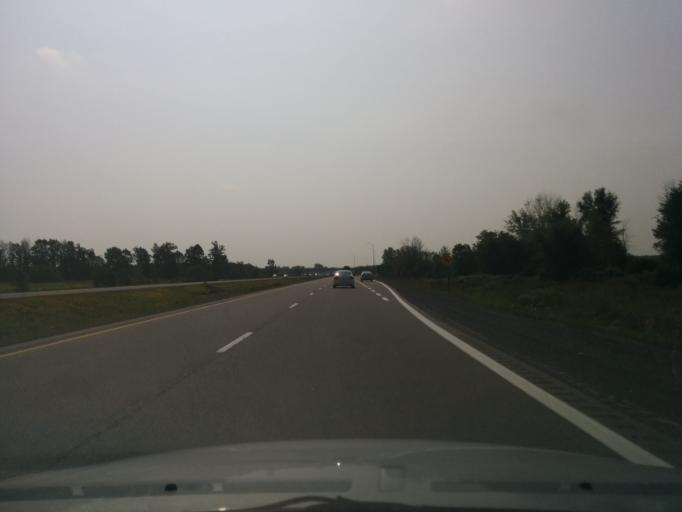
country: CA
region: Ontario
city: Bells Corners
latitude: 45.1523
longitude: -75.6834
